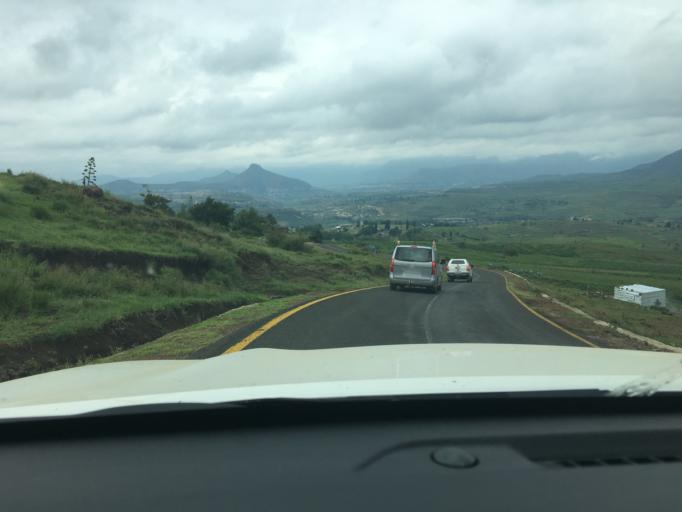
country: LS
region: Berea
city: Teyateyaneng
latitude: -29.2563
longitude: 27.8419
